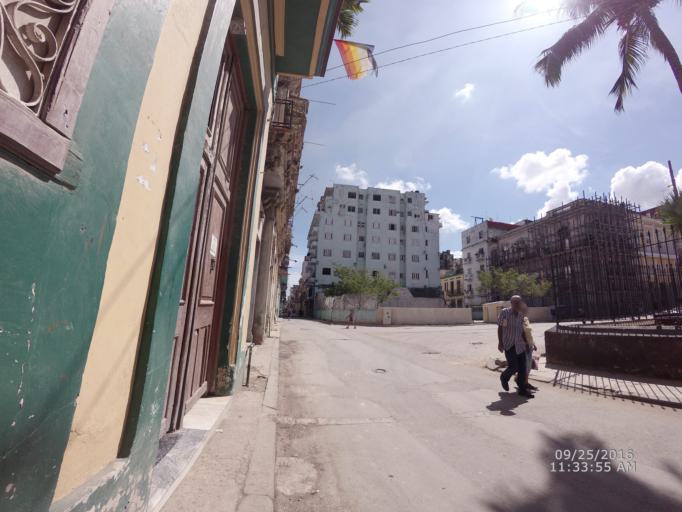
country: CU
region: La Habana
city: La Habana Vieja
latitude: 23.1365
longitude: -82.3562
